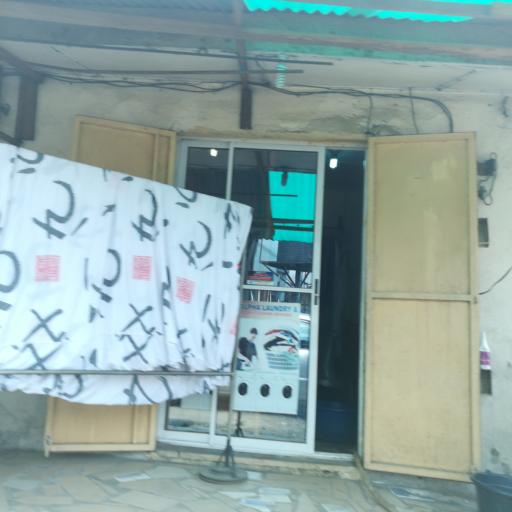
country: NG
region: Rivers
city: Port Harcourt
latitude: 4.7792
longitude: 7.0402
